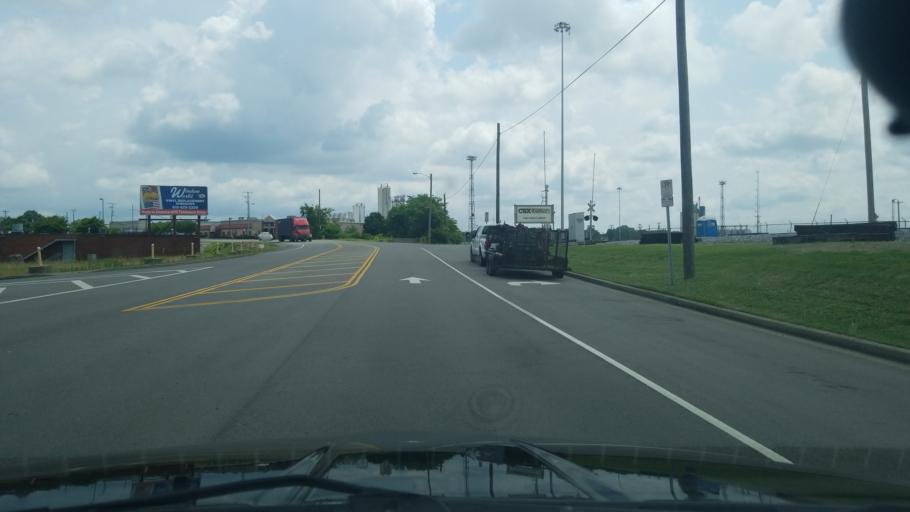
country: US
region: Tennessee
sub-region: Davidson County
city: Oak Hill
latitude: 36.0942
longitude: -86.7582
